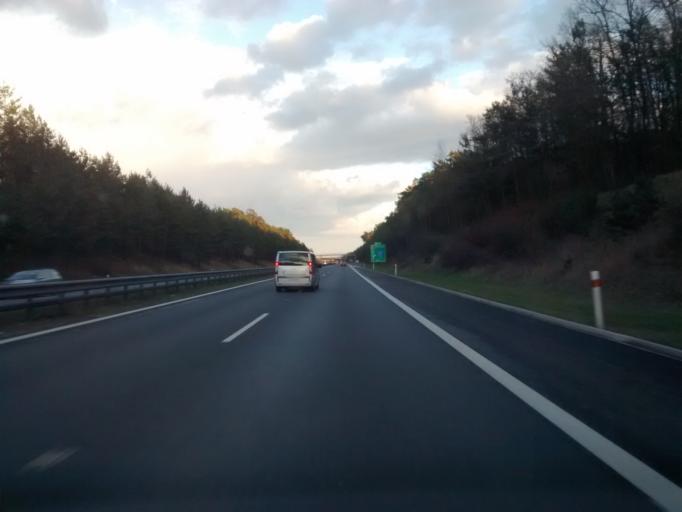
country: CZ
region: Central Bohemia
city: Poricany
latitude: 50.1226
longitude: 14.9305
